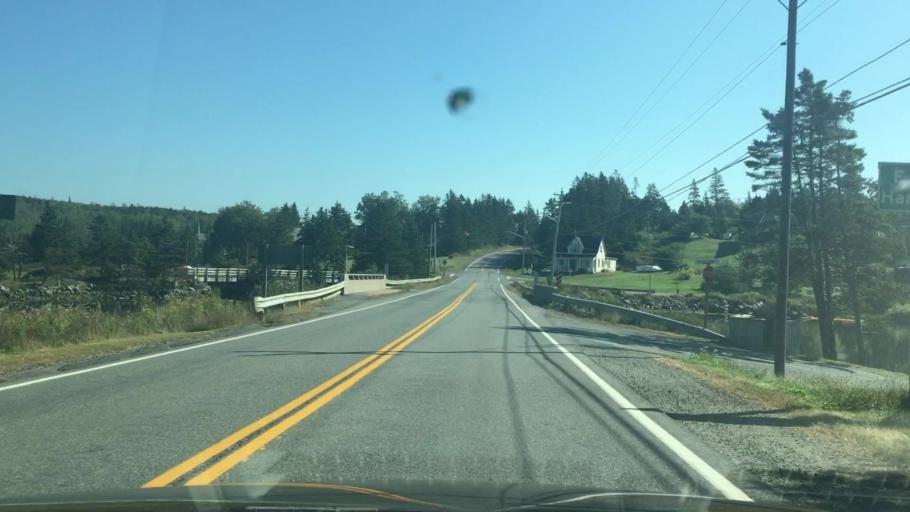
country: CA
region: Nova Scotia
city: Cole Harbour
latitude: 44.7786
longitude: -63.0093
